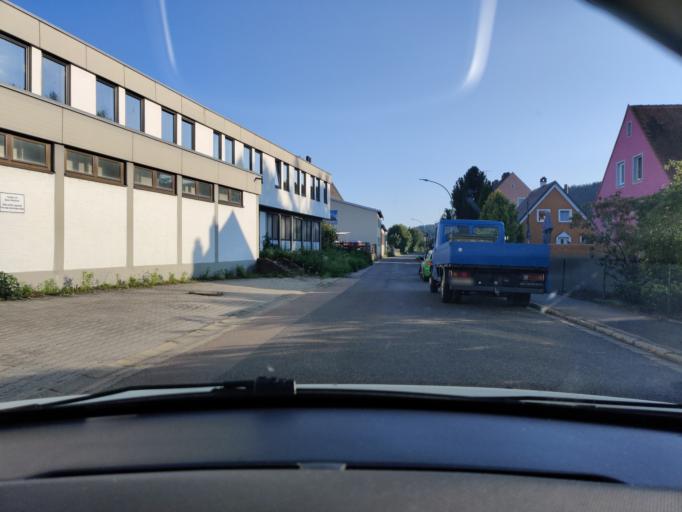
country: DE
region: Bavaria
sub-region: Upper Palatinate
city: Nabburg
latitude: 49.4479
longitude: 12.1796
